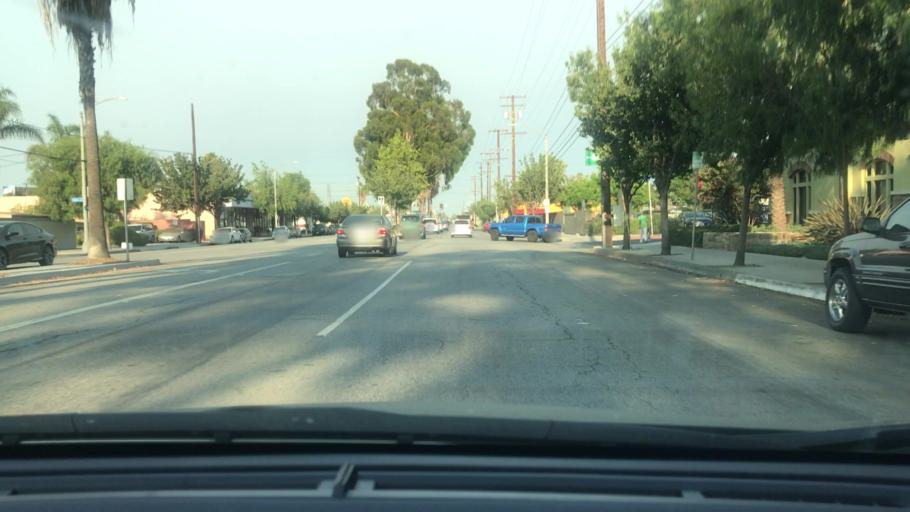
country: US
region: California
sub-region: Los Angeles County
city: Paramount
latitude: 33.8747
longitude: -118.1540
